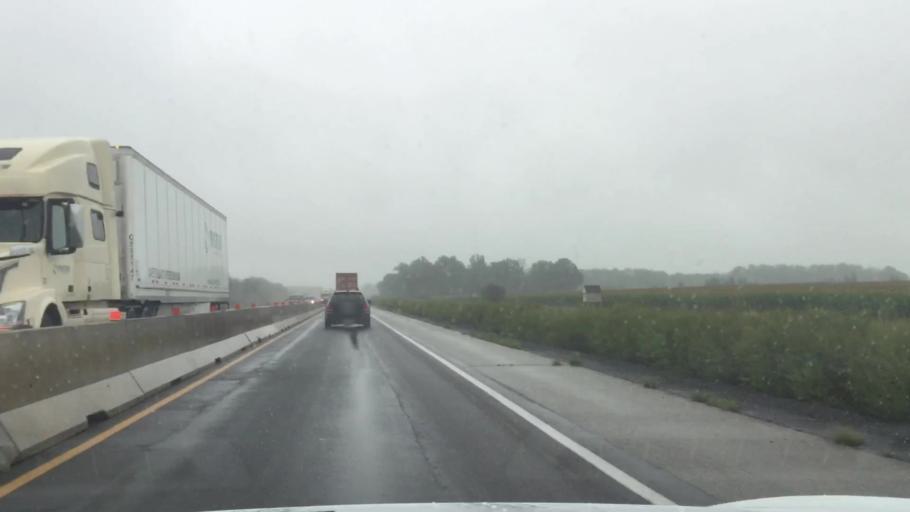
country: CA
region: Ontario
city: Delaware
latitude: 42.7878
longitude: -81.3572
